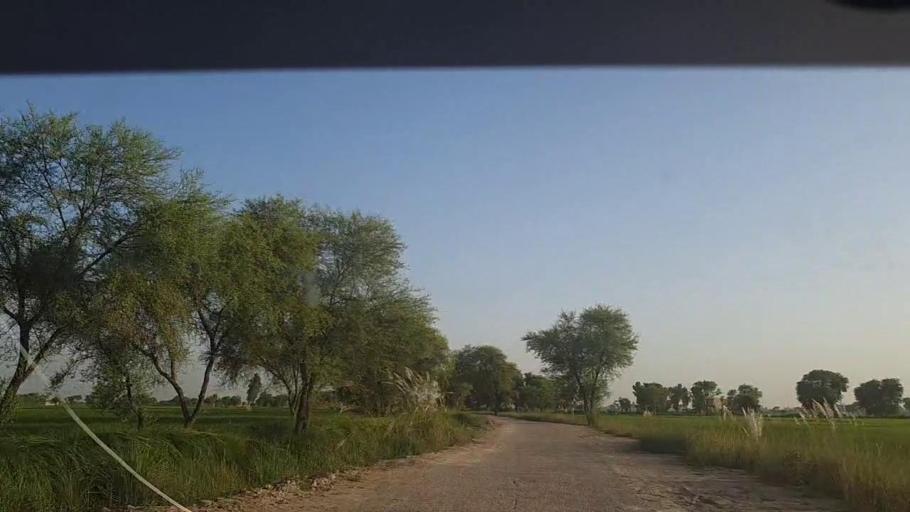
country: PK
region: Sindh
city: Thul
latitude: 28.1257
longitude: 68.8938
